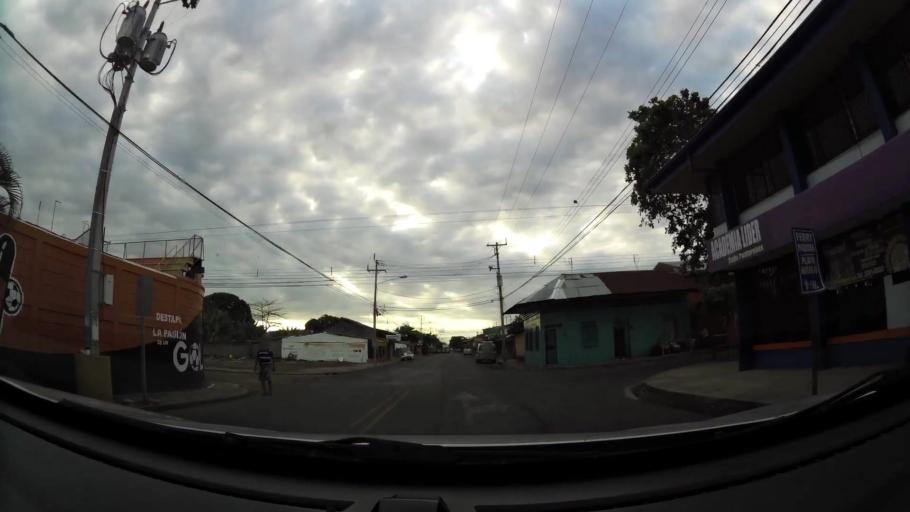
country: CR
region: Puntarenas
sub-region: Canton Central de Puntarenas
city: Puntarenas
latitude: 9.9768
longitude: -84.8394
